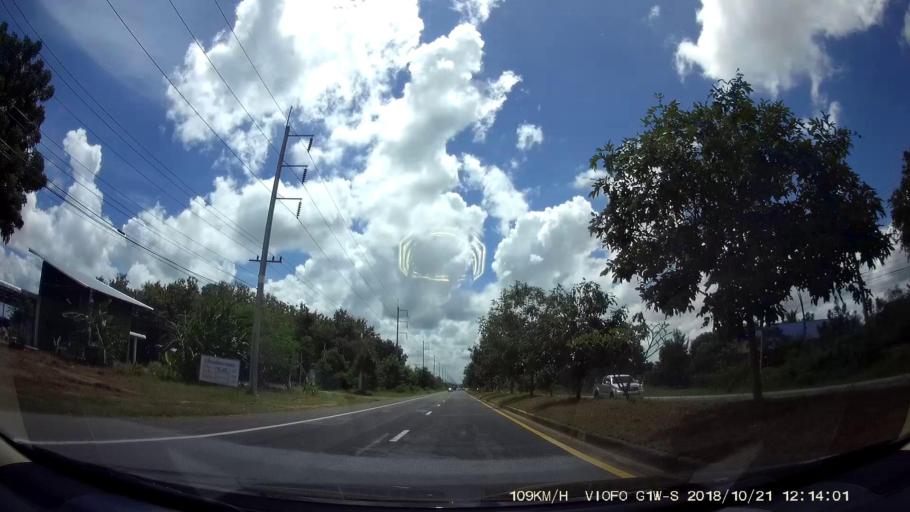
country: TH
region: Chaiyaphum
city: Chatturat
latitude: 15.3841
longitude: 101.8372
